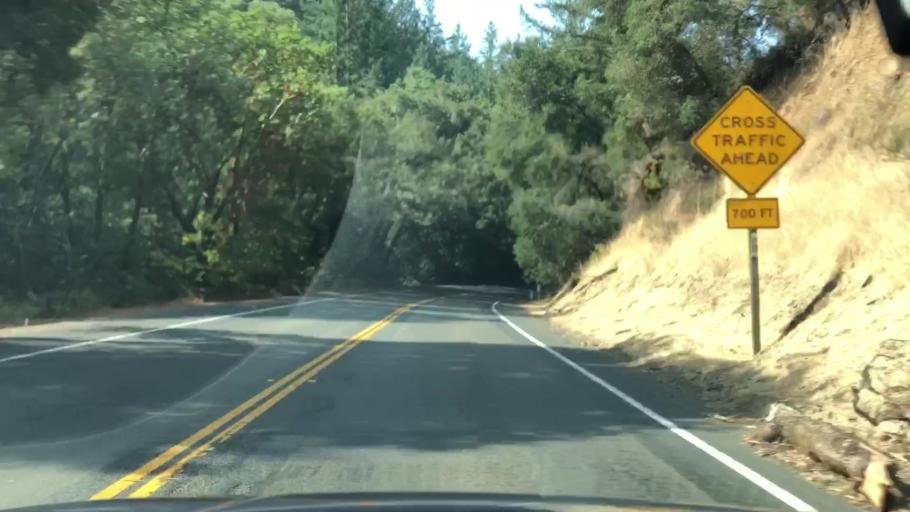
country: US
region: California
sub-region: Napa County
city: Calistoga
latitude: 38.5561
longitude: -122.6365
